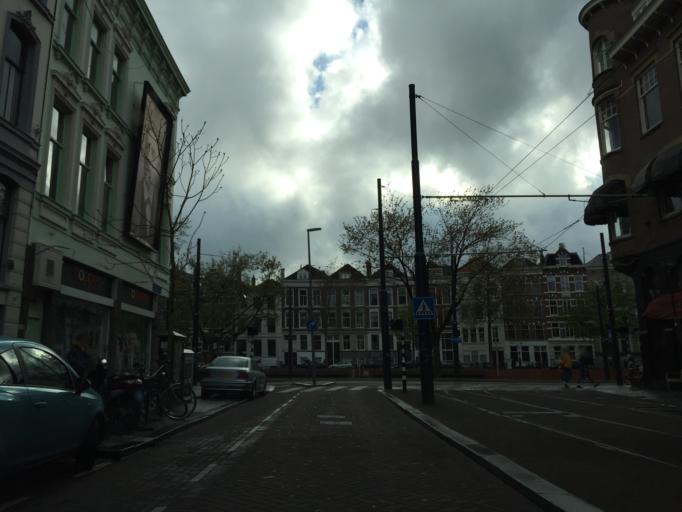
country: NL
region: South Holland
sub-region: Gemeente Rotterdam
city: Rotterdam
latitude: 51.9189
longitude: 4.4730
